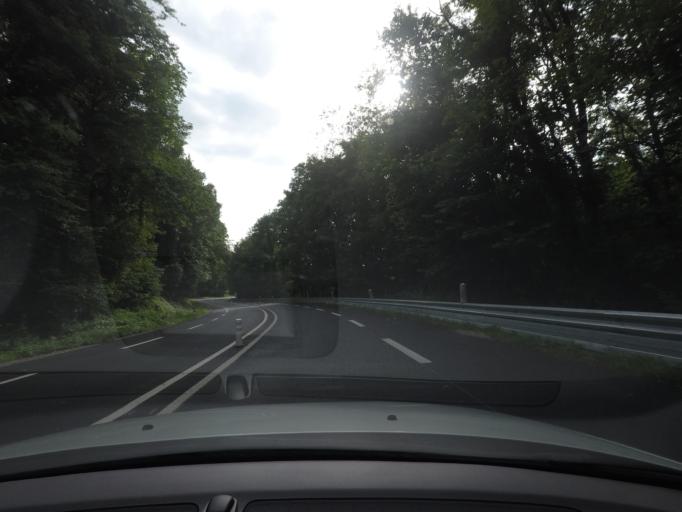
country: FR
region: Haute-Normandie
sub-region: Departement de la Seine-Maritime
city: Les Authieux-sur-le-Port-Saint-Ouen
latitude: 49.3535
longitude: 1.1370
